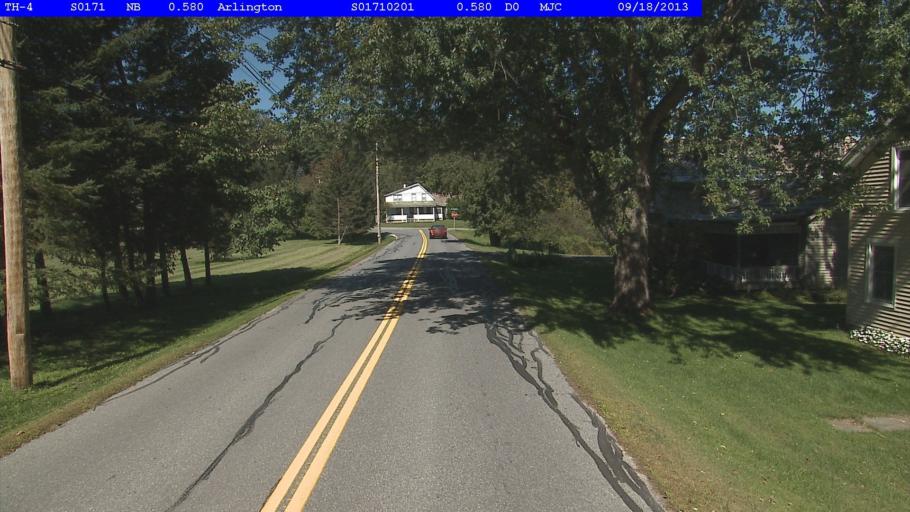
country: US
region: Vermont
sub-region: Bennington County
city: Arlington
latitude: 43.0615
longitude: -73.1470
